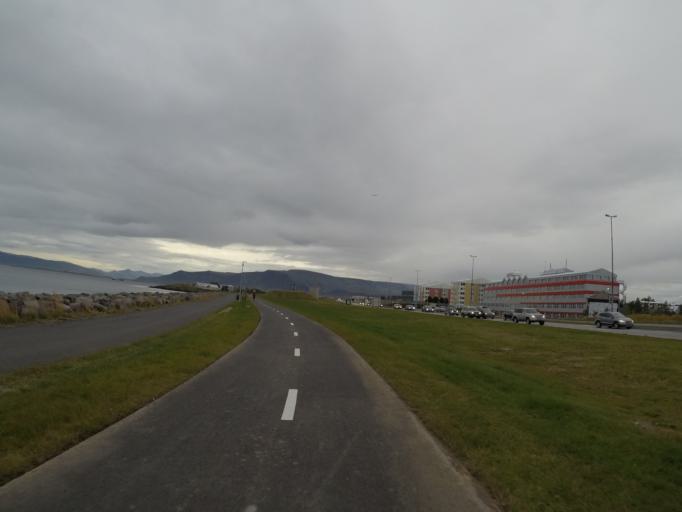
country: IS
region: Capital Region
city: Reykjavik
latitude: 64.1485
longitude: -21.8918
